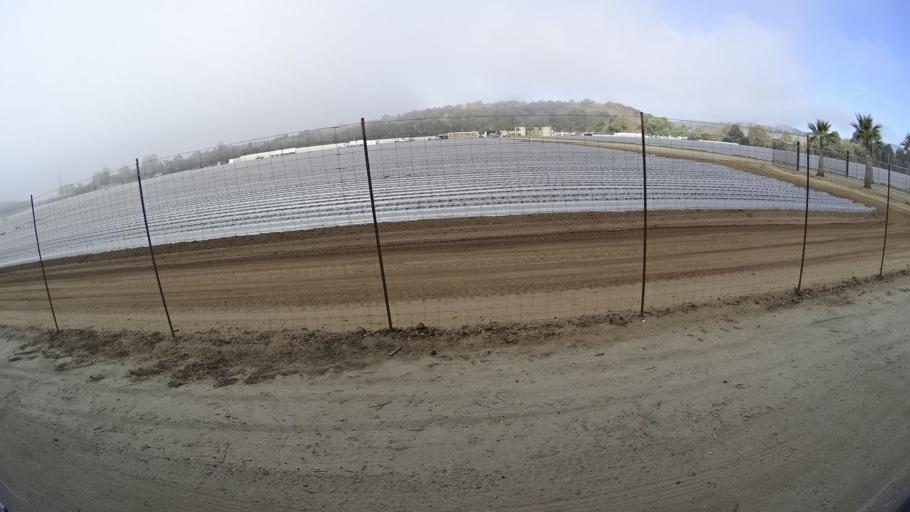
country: US
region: California
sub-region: Monterey County
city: Prunedale
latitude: 36.7780
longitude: -121.5867
